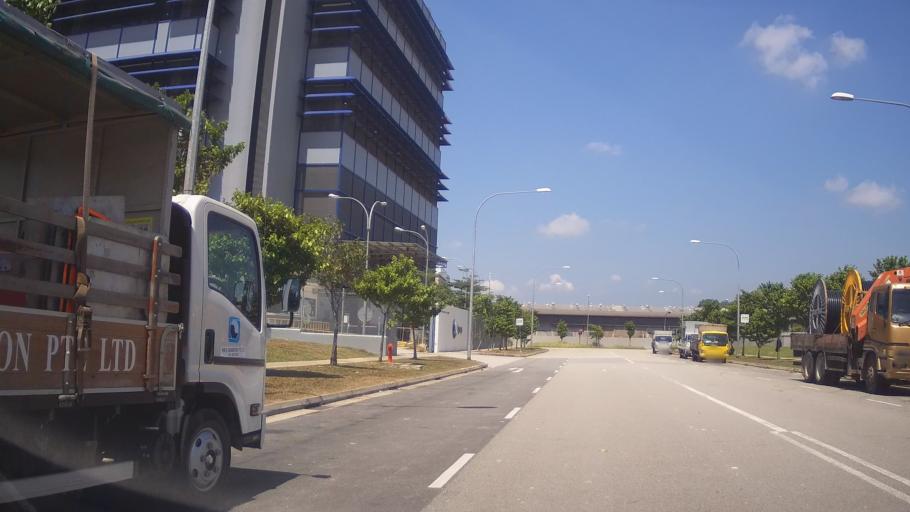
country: SG
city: Singapore
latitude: 1.3177
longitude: 103.7237
